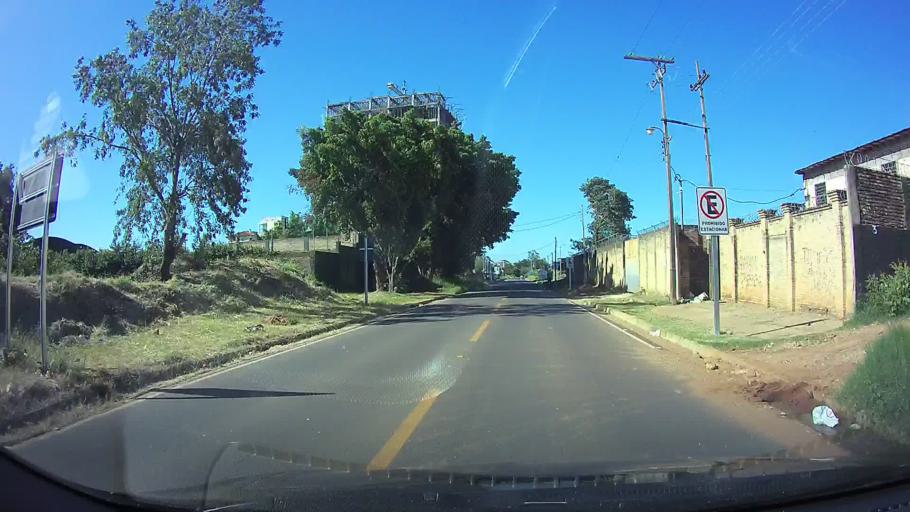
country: PY
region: Central
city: Fernando de la Mora
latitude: -25.2901
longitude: -57.5424
